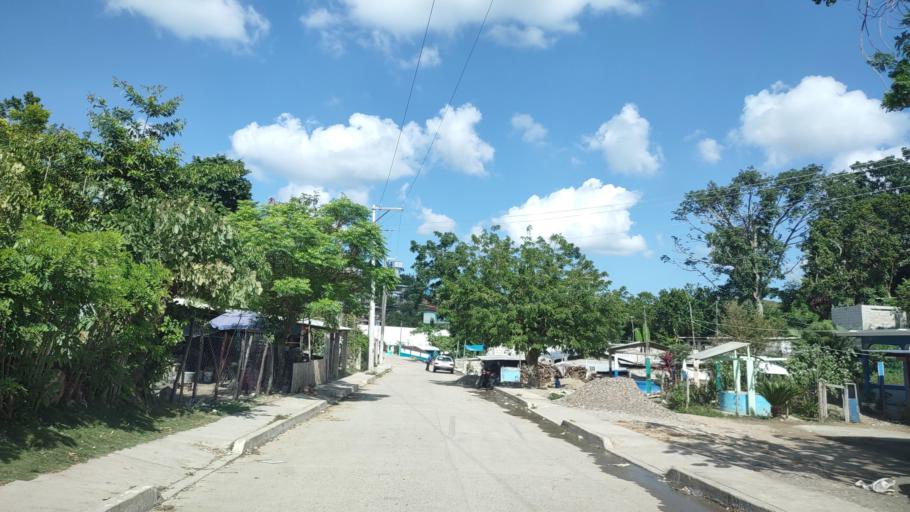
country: MM
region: Shan
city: Taunggyi
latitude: 20.5833
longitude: 97.3763
